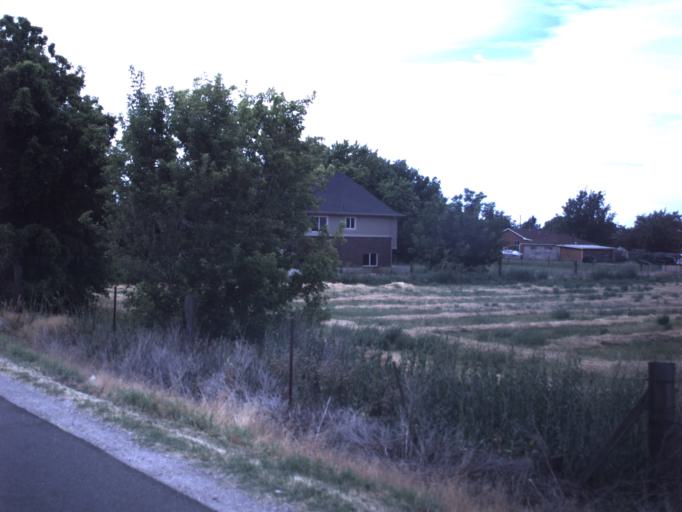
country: US
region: Utah
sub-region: Davis County
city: Clinton
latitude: 41.1649
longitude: -112.0645
